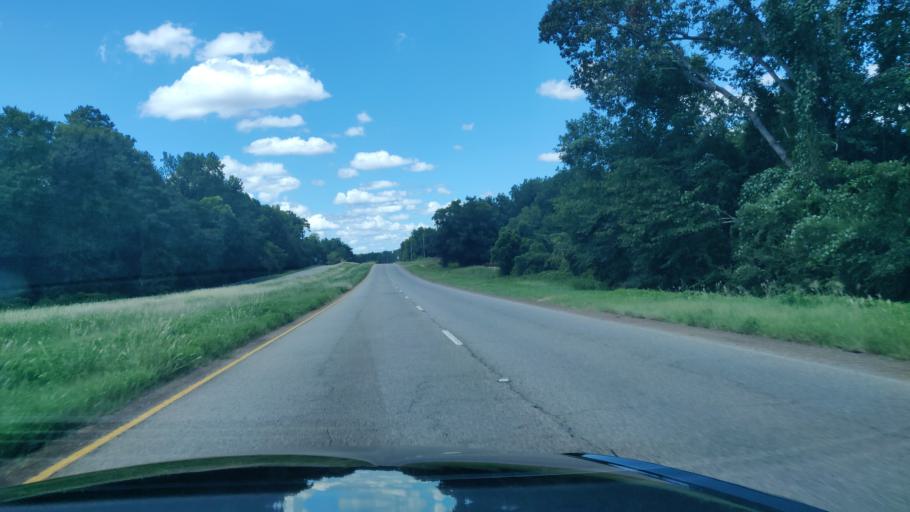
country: US
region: Georgia
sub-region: Stewart County
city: Richland
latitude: 32.0443
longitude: -84.6757
